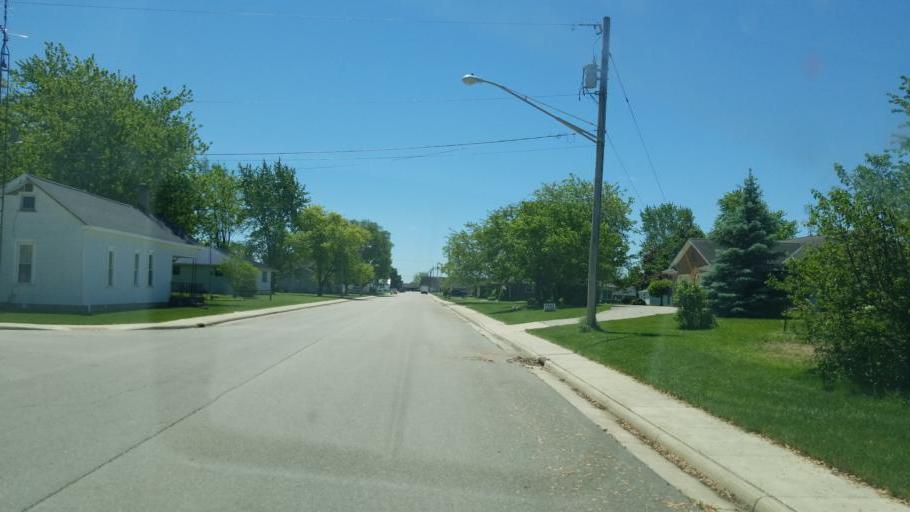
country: US
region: Ohio
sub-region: Mercer County
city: Saint Henry
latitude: 40.3550
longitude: -84.6429
